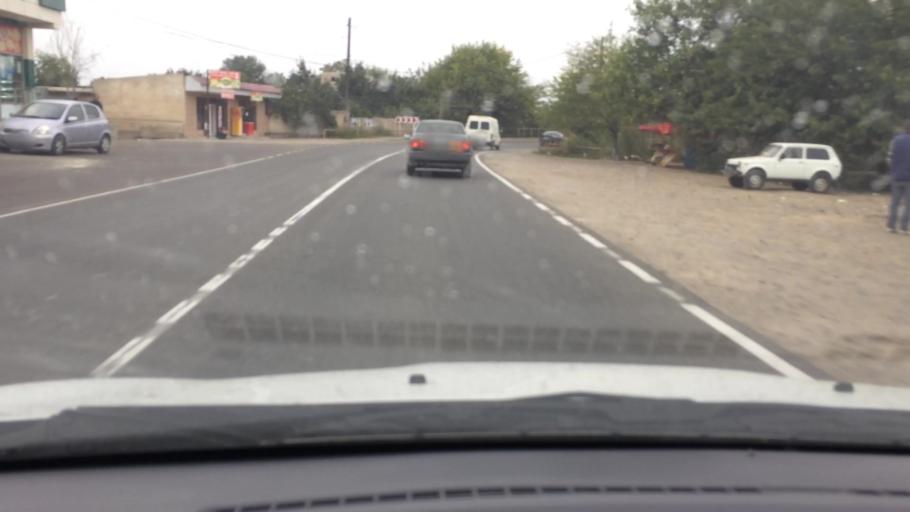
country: GE
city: Naghvarevi
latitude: 41.3992
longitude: 44.8246
